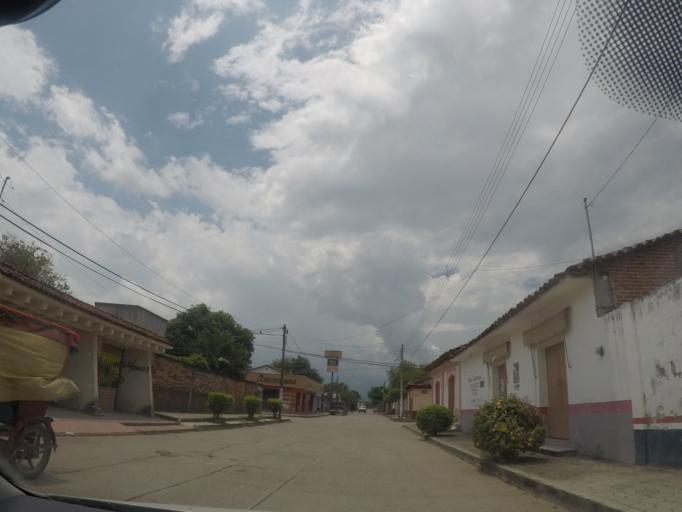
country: MX
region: Oaxaca
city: Santo Domingo Zanatepec
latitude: 16.4813
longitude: -94.3536
